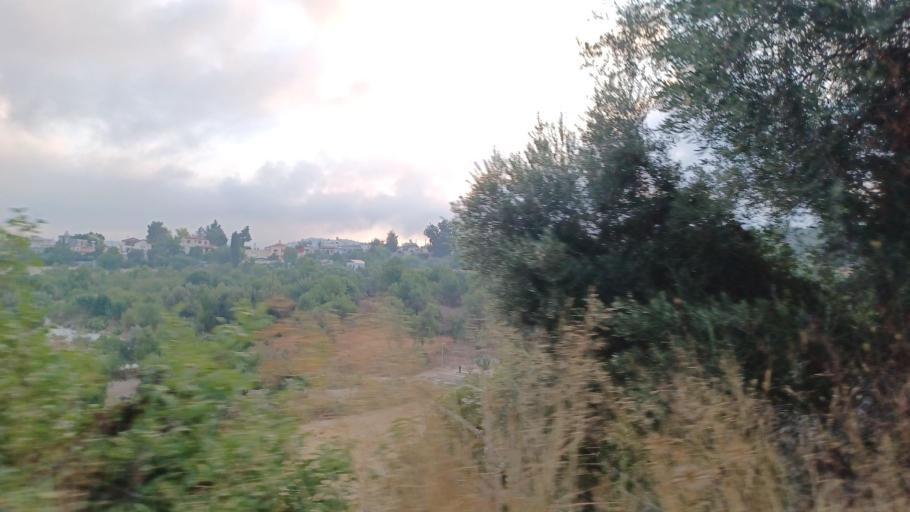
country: CY
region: Pafos
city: Mesogi
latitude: 34.8215
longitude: 32.5798
